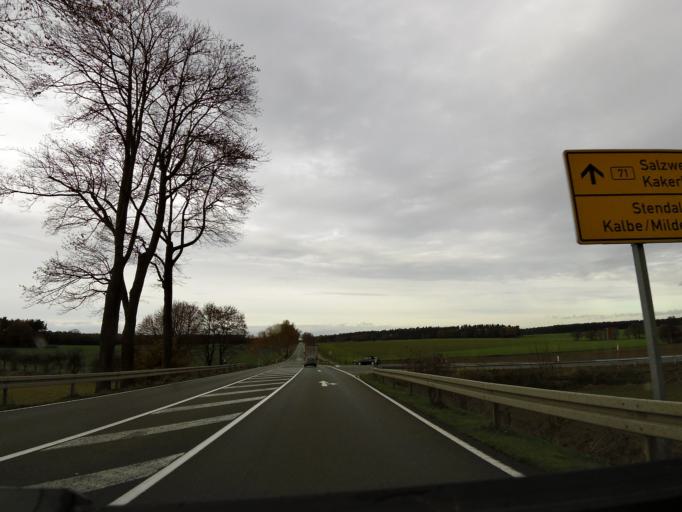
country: DE
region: Saxony-Anhalt
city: Kalbe
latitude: 52.6480
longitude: 11.2977
